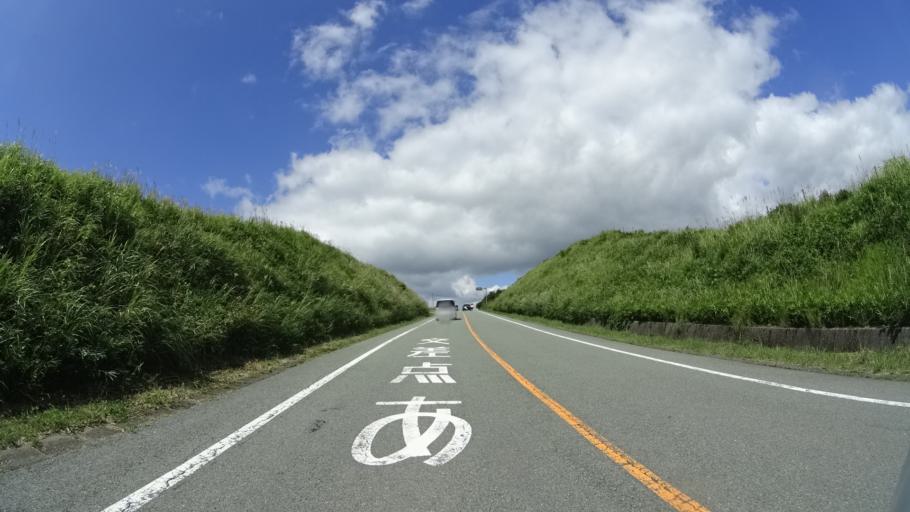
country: JP
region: Kumamoto
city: Aso
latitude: 33.0004
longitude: 131.0738
